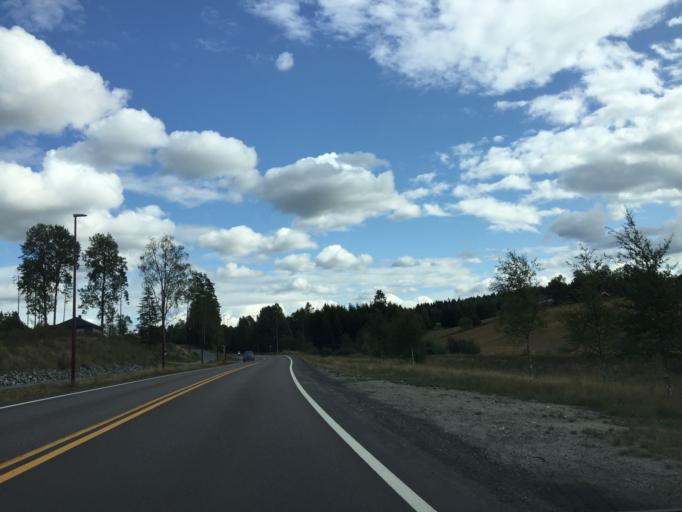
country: NO
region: Ostfold
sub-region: Hobol
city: Knappstad
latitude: 59.6209
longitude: 11.0067
